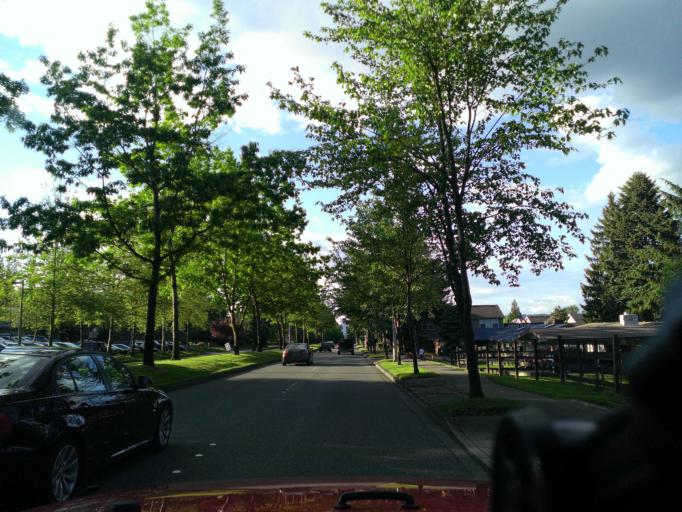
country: US
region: Washington
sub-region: King County
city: Redmond
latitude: 47.6687
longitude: -122.1430
